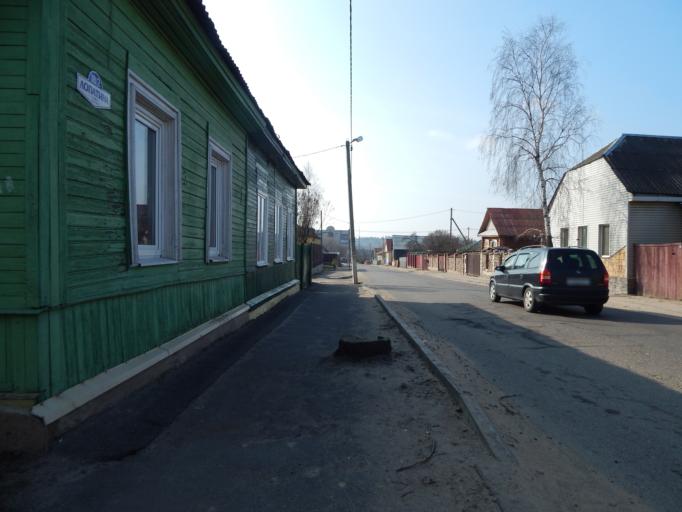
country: BY
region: Minsk
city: Horad Barysaw
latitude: 54.2439
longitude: 28.5028
